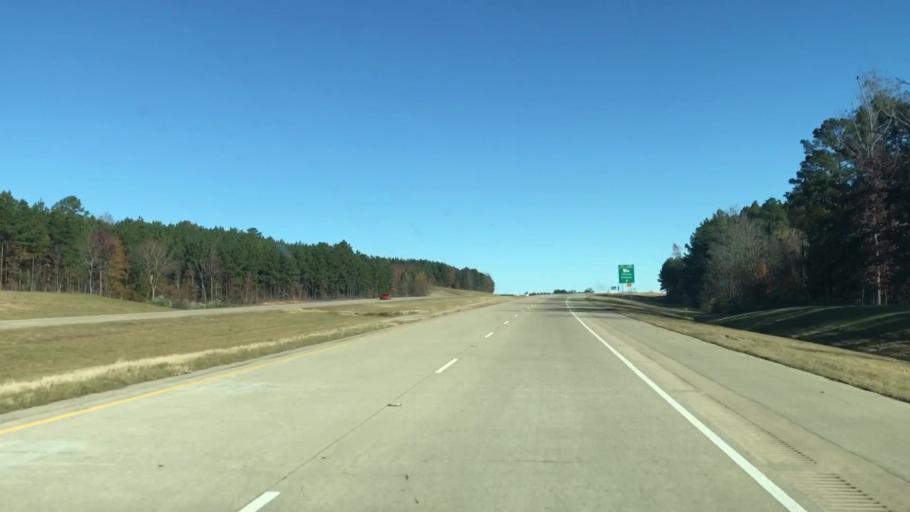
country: US
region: Louisiana
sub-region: Caddo Parish
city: Oil City
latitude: 32.8071
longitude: -93.8850
